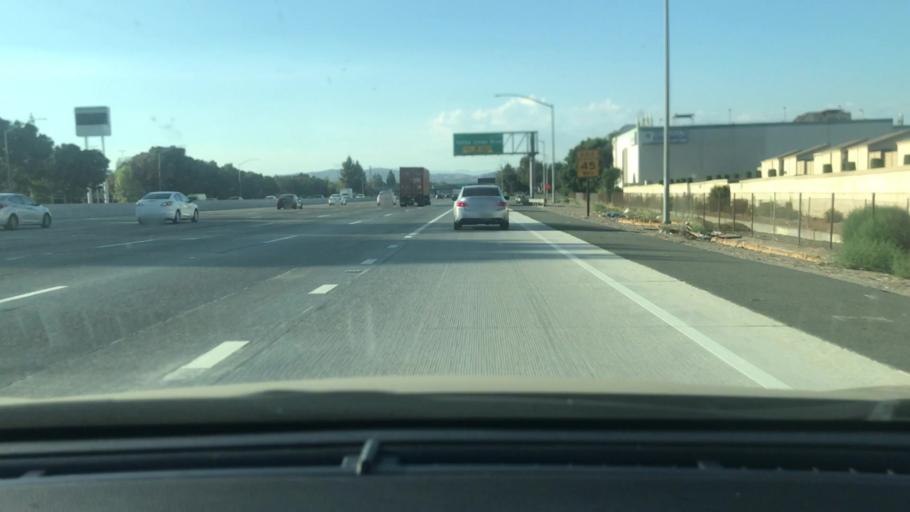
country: US
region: California
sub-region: Orange County
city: Placentia
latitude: 33.8519
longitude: -117.8779
